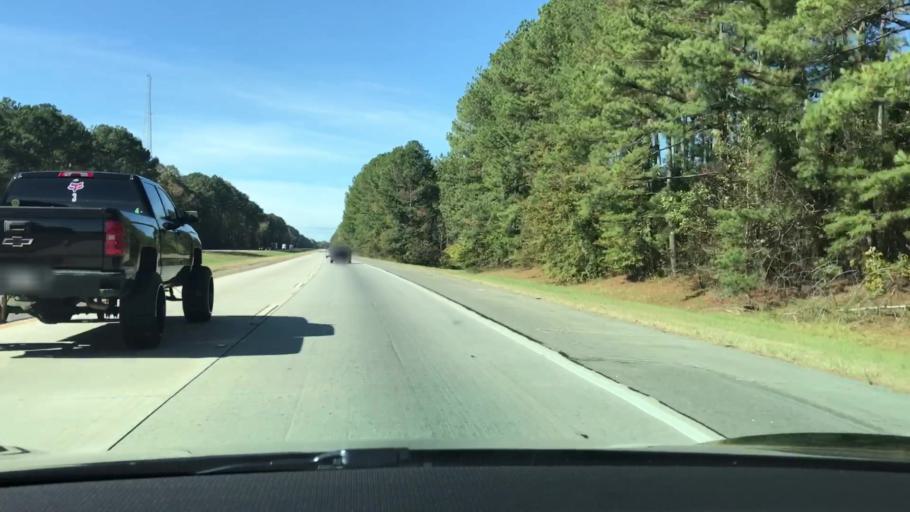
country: US
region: Georgia
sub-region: Taliaferro County
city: Crawfordville
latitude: 33.5305
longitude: -82.9318
